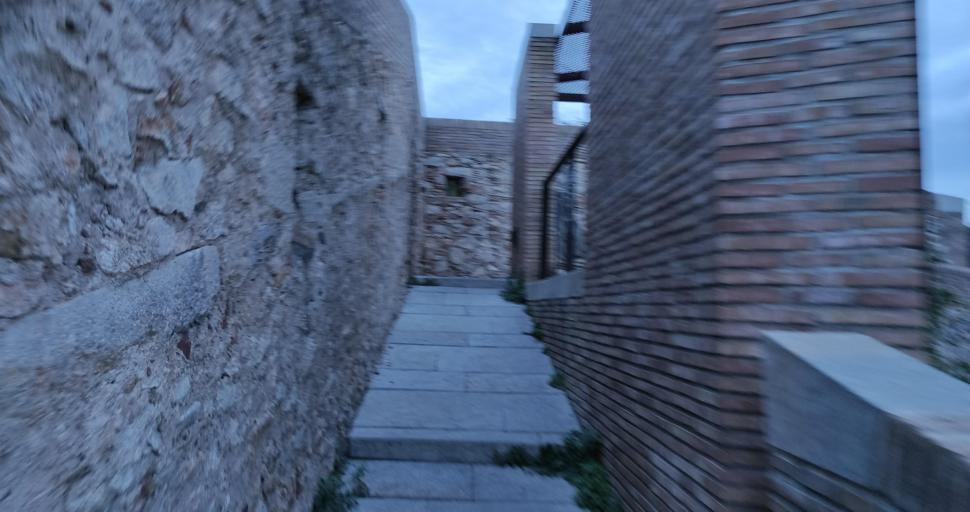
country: ES
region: Catalonia
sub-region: Provincia de Girona
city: Girona
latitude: 41.9897
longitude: 2.8273
